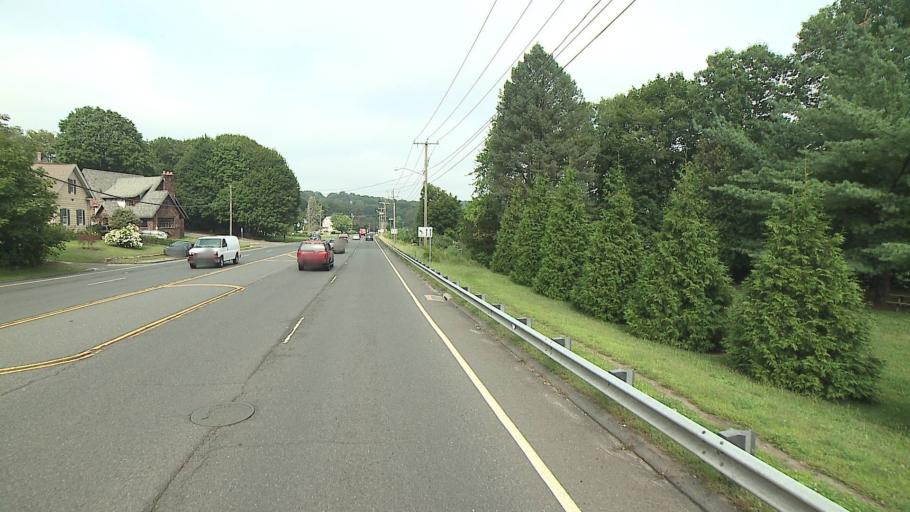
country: US
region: Connecticut
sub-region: New Haven County
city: Waterbury
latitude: 41.5737
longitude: -73.0648
